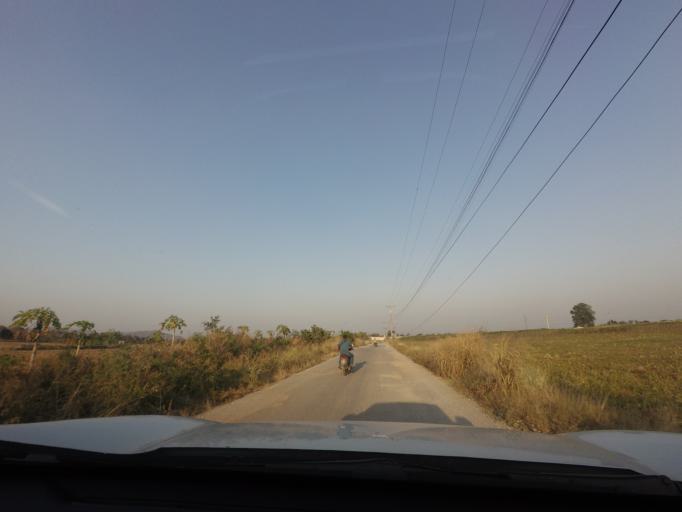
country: TH
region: Nakhon Ratchasima
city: Pak Chong
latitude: 14.6444
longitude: 101.3750
